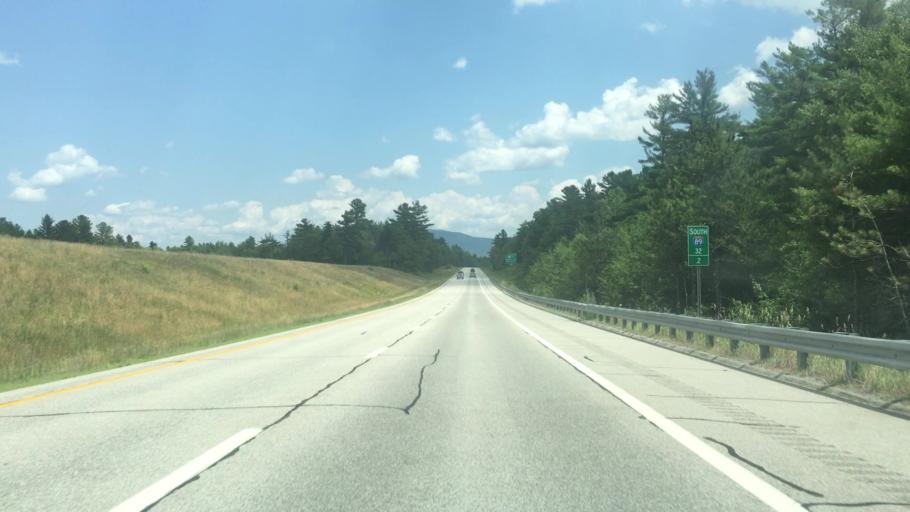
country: US
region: New Hampshire
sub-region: Merrimack County
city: New London
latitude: 43.3951
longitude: -72.0011
